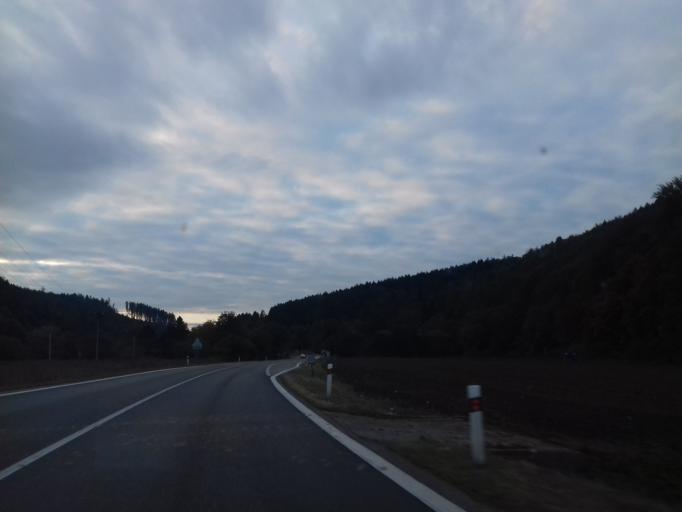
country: CZ
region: Zlin
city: Bojkovice
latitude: 48.9491
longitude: 17.9023
